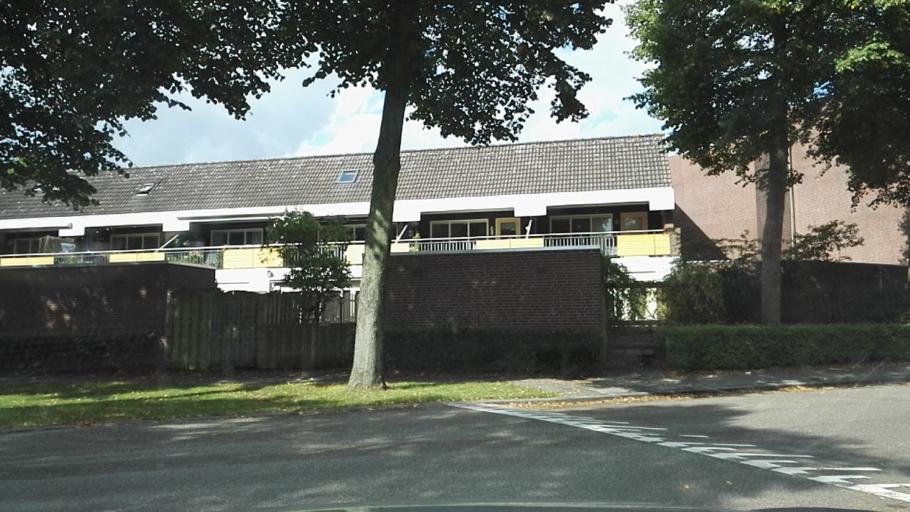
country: NL
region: Gelderland
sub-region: Gemeente Apeldoorn
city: Apeldoorn
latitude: 52.2024
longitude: 5.9872
